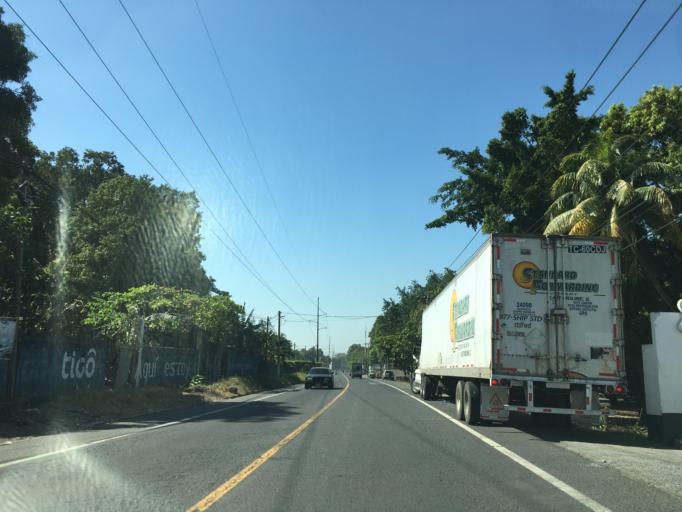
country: GT
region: Escuintla
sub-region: Municipio de Escuintla
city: Escuintla
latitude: 14.2761
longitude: -90.7908
